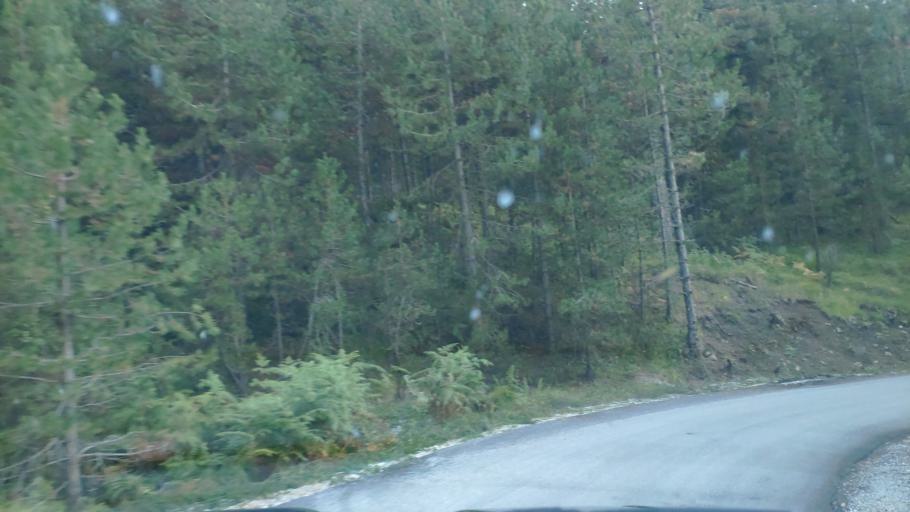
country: AL
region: Korce
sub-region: Rrethi i Kolonjes
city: Erseke
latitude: 40.2937
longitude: 20.8622
